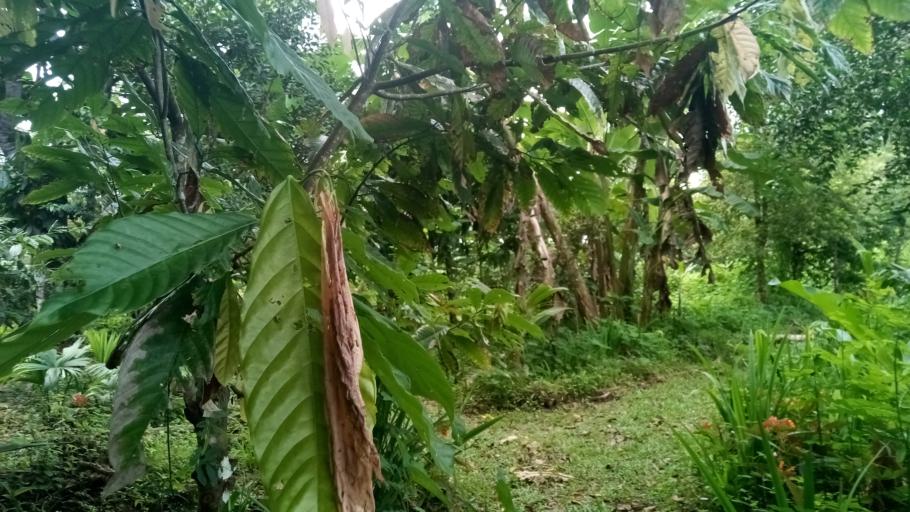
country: CR
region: Limon
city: Sixaola
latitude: 9.6232
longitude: -82.6203
